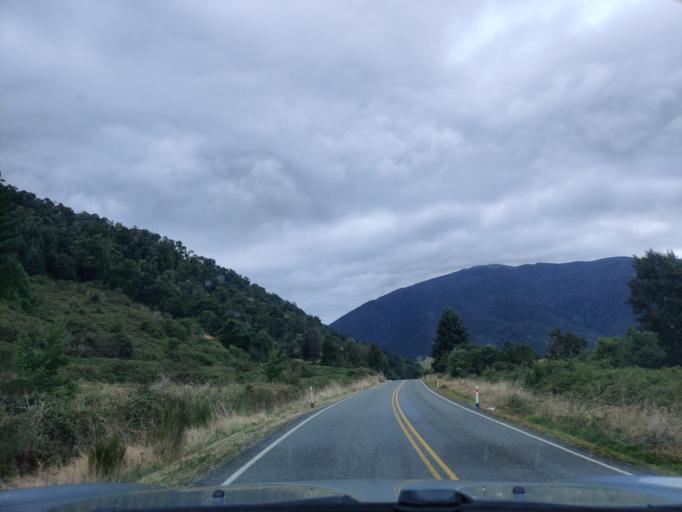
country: NZ
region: Tasman
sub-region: Tasman District
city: Wakefield
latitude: -41.6899
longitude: 172.4682
